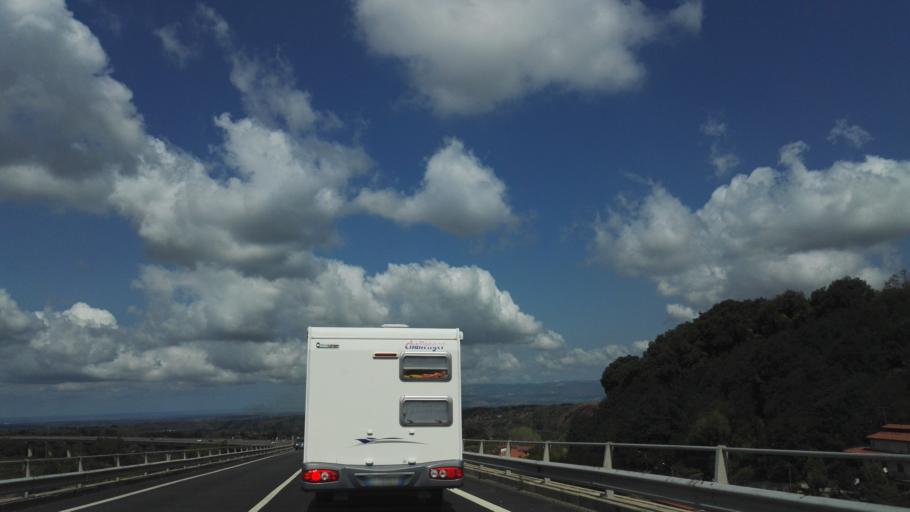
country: IT
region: Calabria
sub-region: Provincia di Reggio Calabria
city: Anoia Superiore
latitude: 38.4190
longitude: 16.1021
